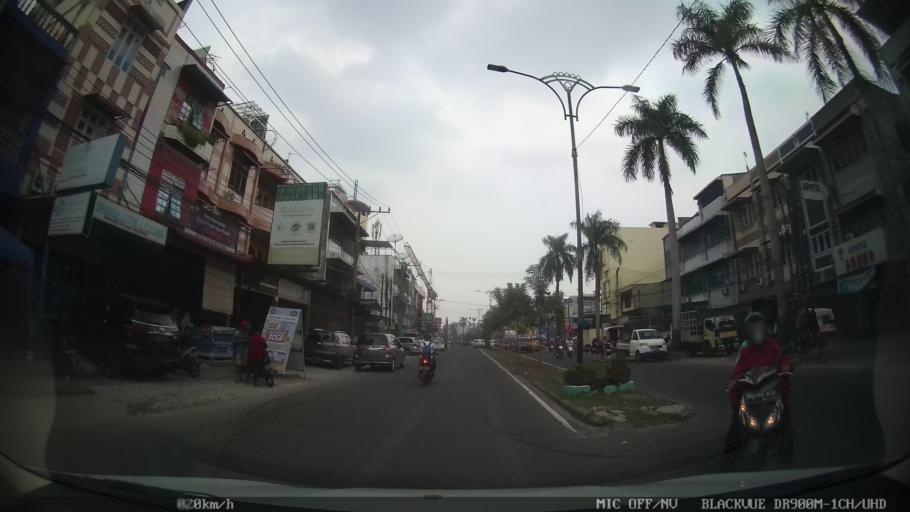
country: ID
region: North Sumatra
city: Medan
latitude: 3.5696
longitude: 98.6867
